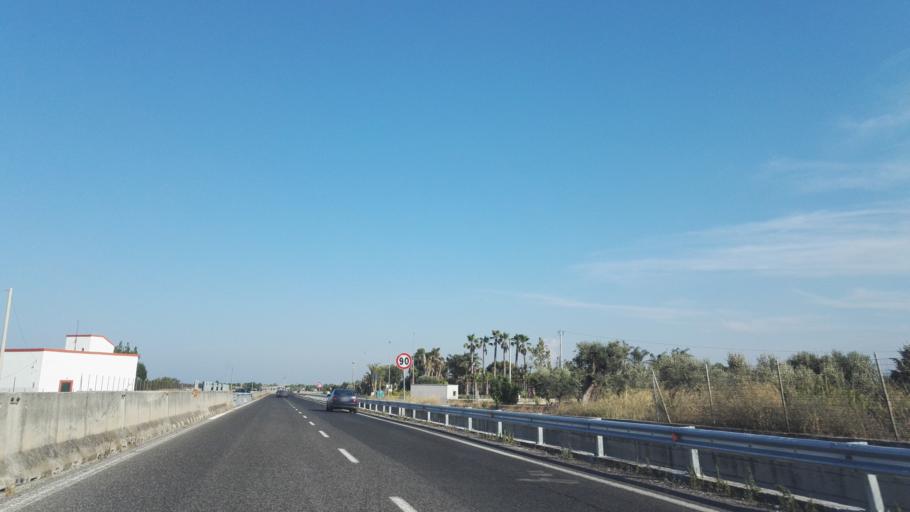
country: IT
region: Apulia
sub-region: Provincia di Bari
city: Monopoli
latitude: 40.9278
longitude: 17.3073
